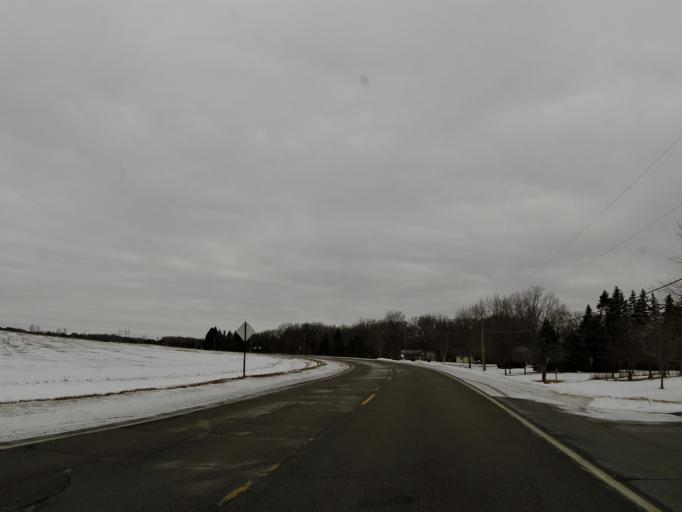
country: US
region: Minnesota
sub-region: Washington County
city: Cottage Grove
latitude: 44.8296
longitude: -92.8883
